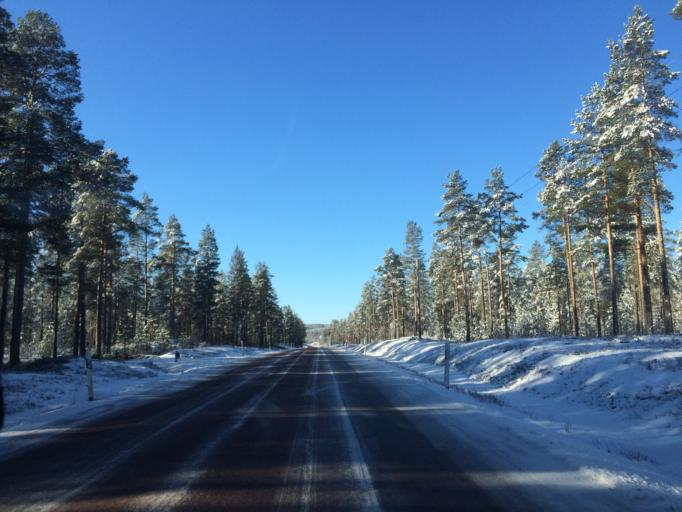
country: SE
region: Dalarna
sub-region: Vansbro Kommun
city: Vansbro
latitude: 60.8439
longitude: 14.1527
